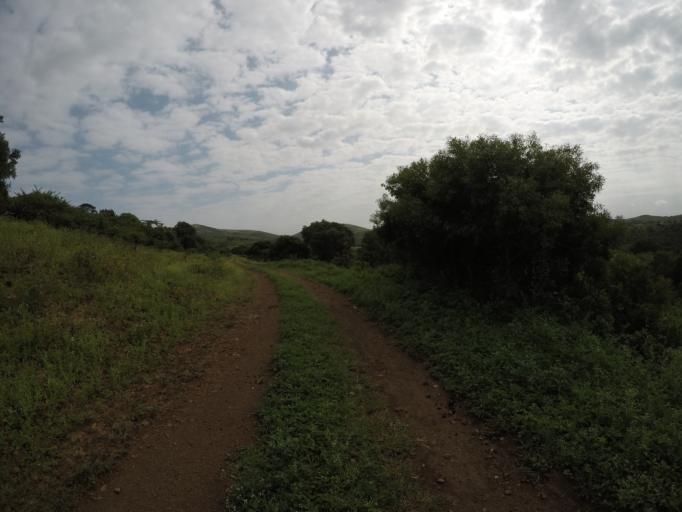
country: ZA
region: KwaZulu-Natal
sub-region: uThungulu District Municipality
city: Empangeni
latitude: -28.6292
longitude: 31.9098
